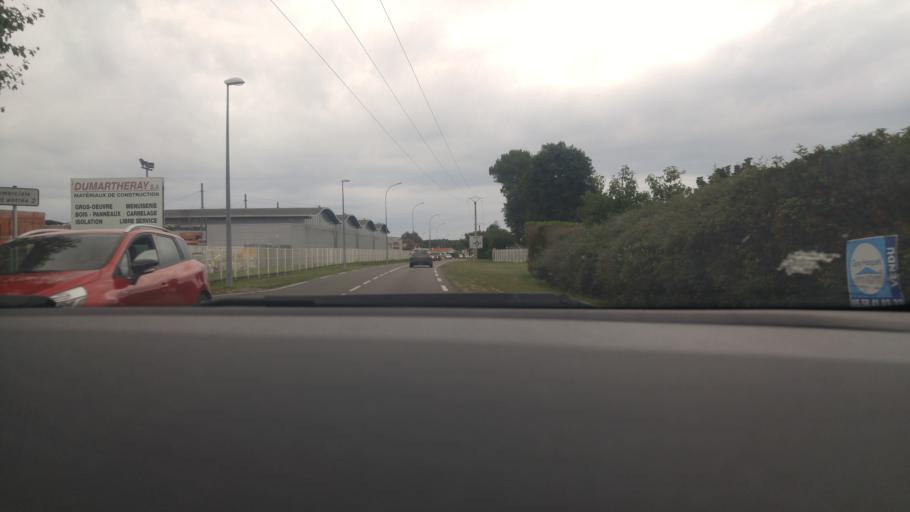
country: FR
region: Aquitaine
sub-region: Departement des Landes
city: Soustons
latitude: 43.7472
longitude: -1.3295
